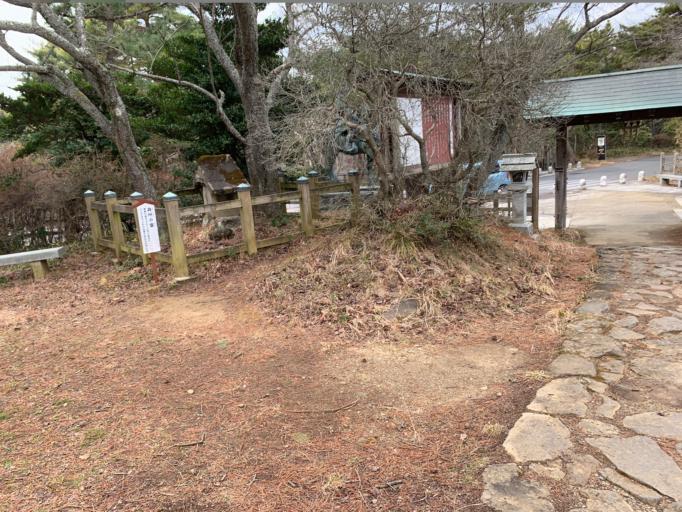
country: JP
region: Ibaraki
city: Kitaibaraki
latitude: 36.8685
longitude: 140.7810
